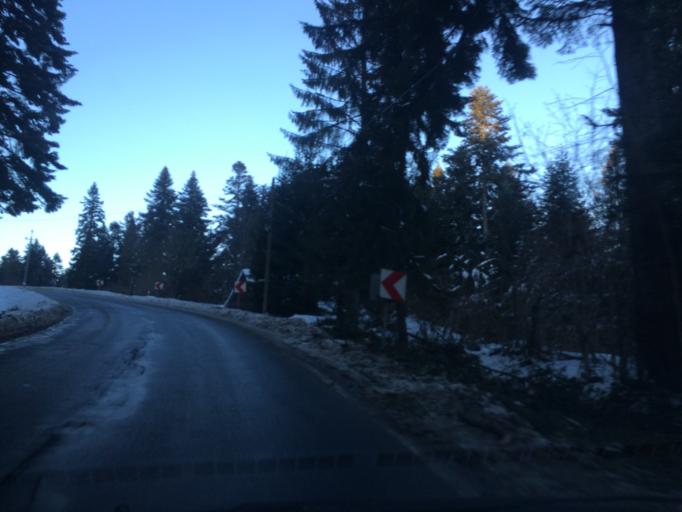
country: PL
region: Subcarpathian Voivodeship
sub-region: Powiat bieszczadzki
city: Lutowiska
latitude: 49.2709
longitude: 22.6871
